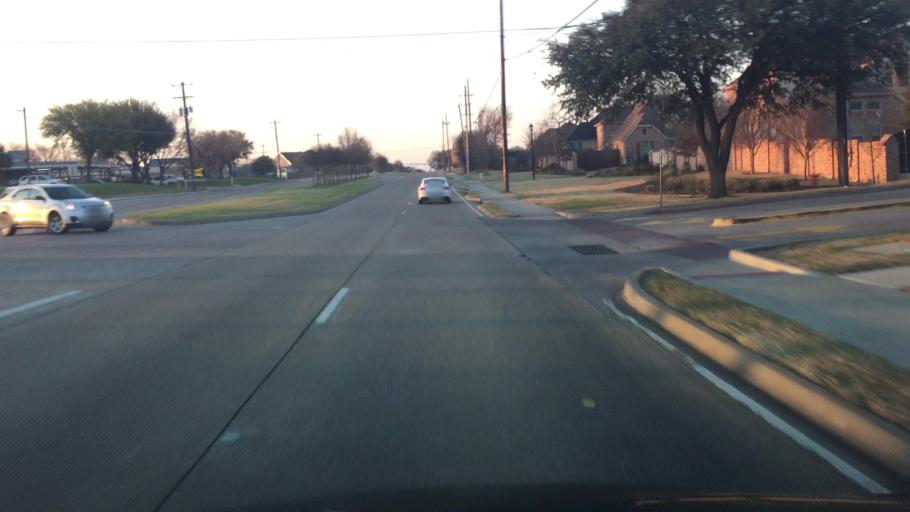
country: US
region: Texas
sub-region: Denton County
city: Highland Village
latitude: 33.0713
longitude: -97.0620
